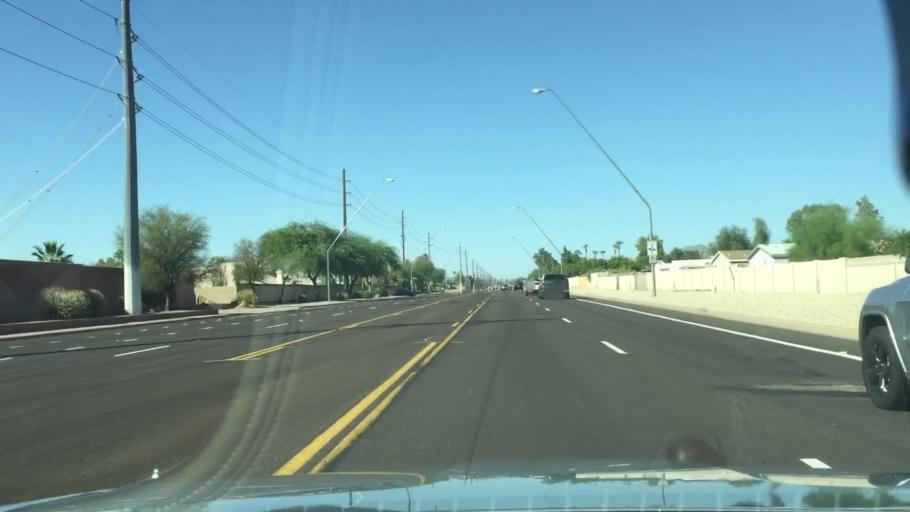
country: US
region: Arizona
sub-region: Pinal County
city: Apache Junction
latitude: 33.3944
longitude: -111.6675
